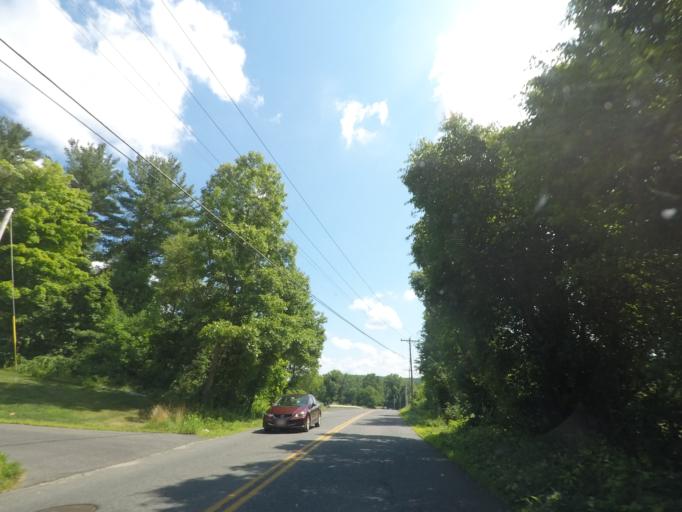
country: US
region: Massachusetts
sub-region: Hampden County
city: Monson
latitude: 42.1206
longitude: -72.3316
